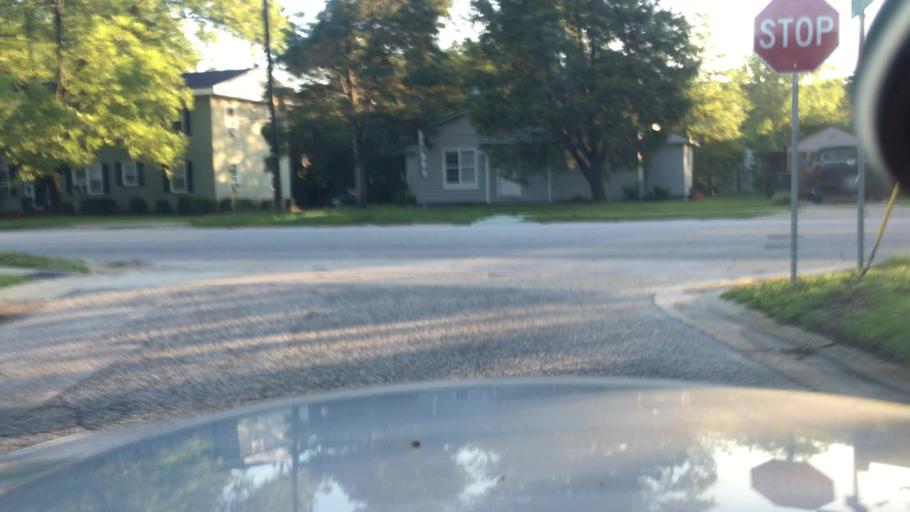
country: US
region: North Carolina
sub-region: Cumberland County
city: Fayetteville
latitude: 35.0630
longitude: -78.9105
